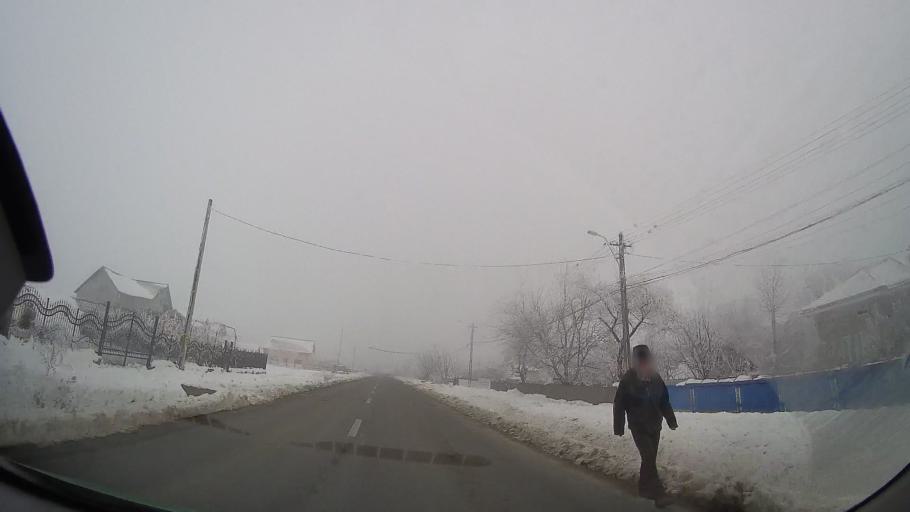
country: RO
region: Iasi
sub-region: Comuna Stolniceni-Prajescu
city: Stolniceni-Prajescu
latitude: 47.2006
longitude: 26.7398
